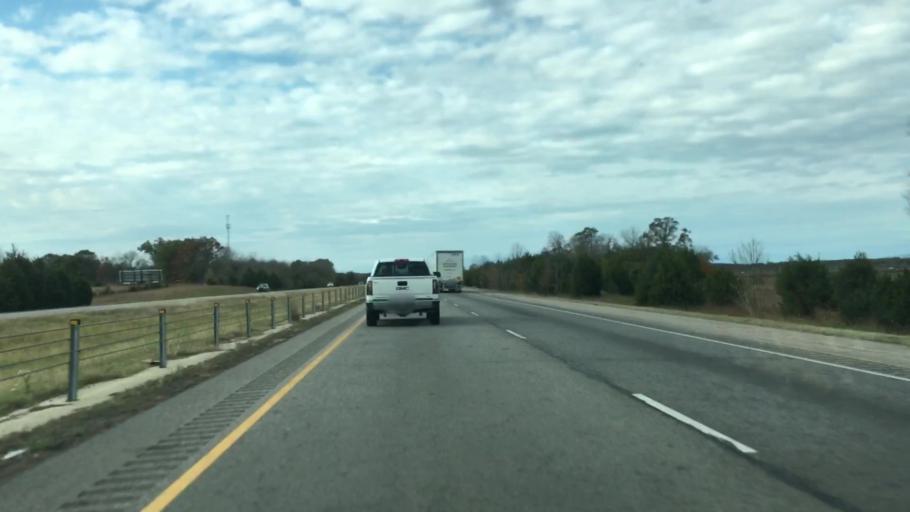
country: US
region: Arkansas
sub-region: Conway County
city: Morrilton
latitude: 35.1997
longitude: -92.8047
